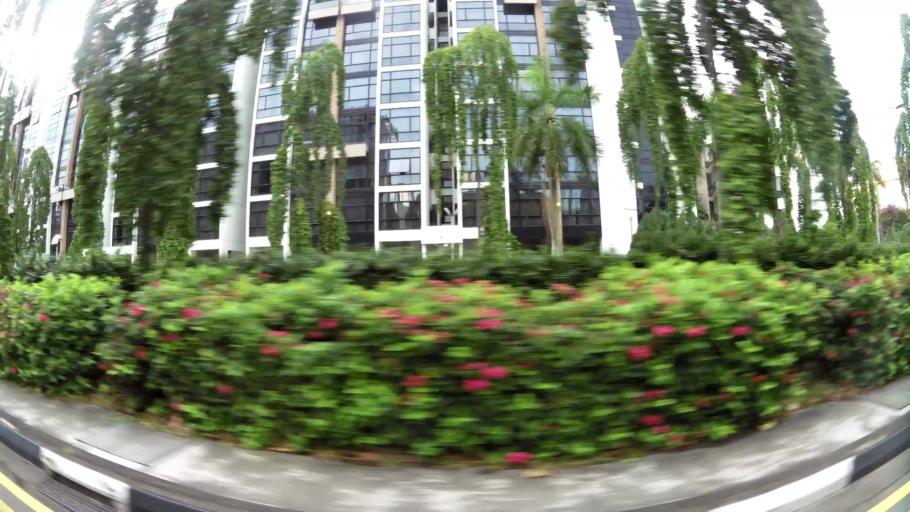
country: SG
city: Singapore
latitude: 1.2898
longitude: 103.8419
